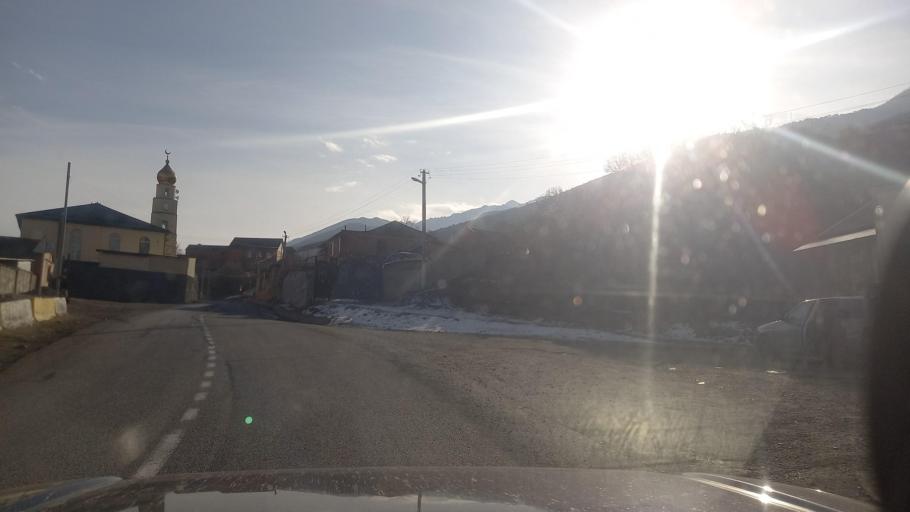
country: RU
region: Ingushetiya
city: Dzhayrakh
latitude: 42.8279
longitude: 44.6689
